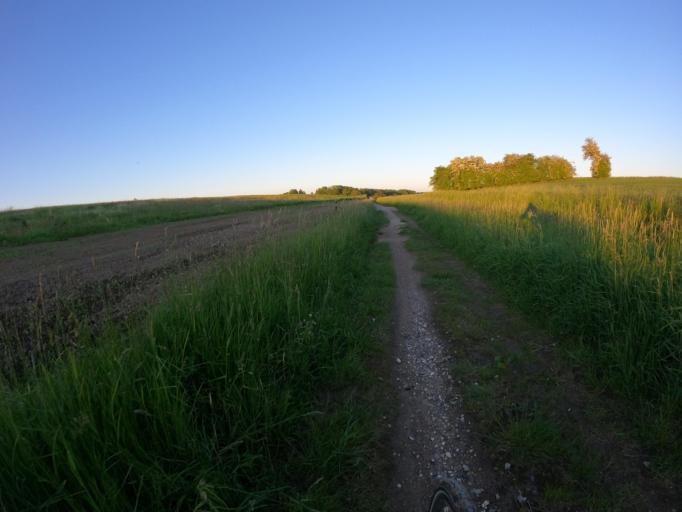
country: DK
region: Capital Region
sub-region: Hoje-Taastrup Kommune
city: Flong
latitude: 55.6258
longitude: 12.2363
